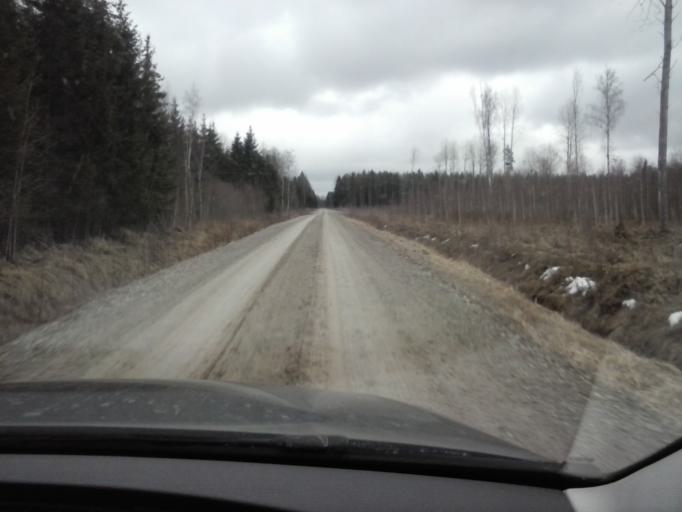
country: EE
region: Jogevamaa
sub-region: Mustvee linn
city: Mustvee
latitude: 59.0598
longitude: 26.8436
